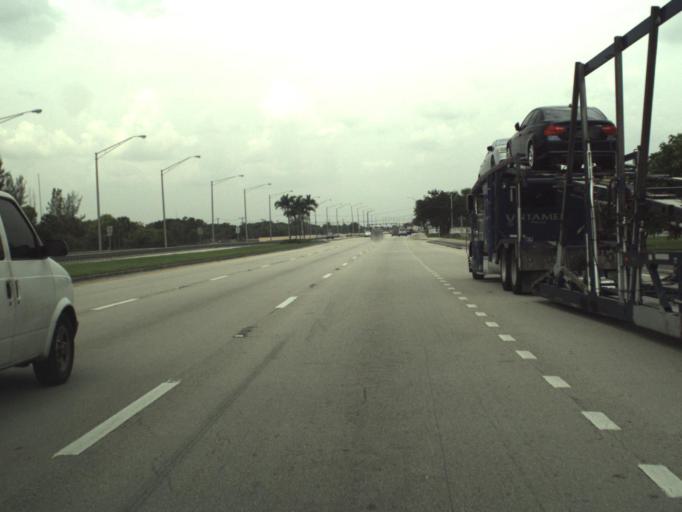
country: US
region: Florida
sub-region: Broward County
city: Lauderhill
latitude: 26.1361
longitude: -80.2060
